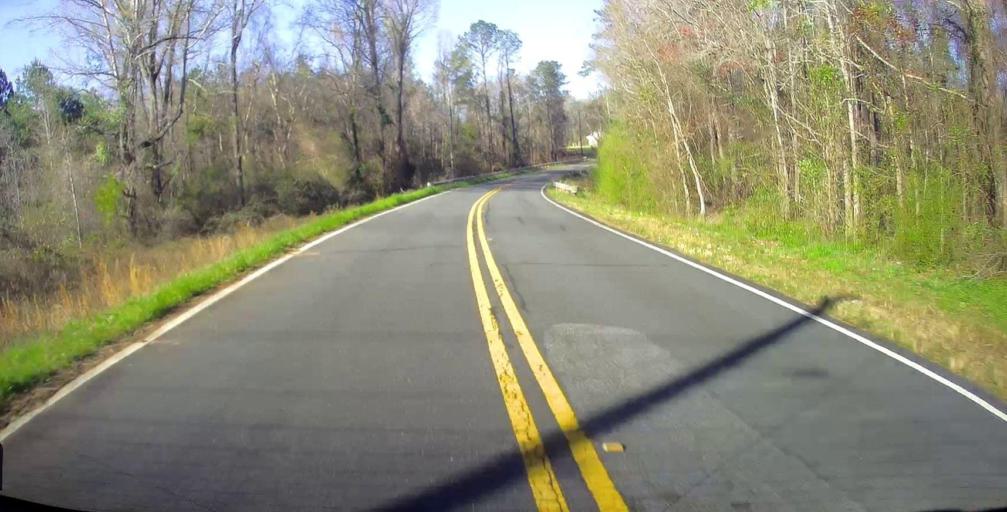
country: US
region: Georgia
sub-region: Peach County
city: Fort Valley
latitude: 32.5191
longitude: -83.9196
